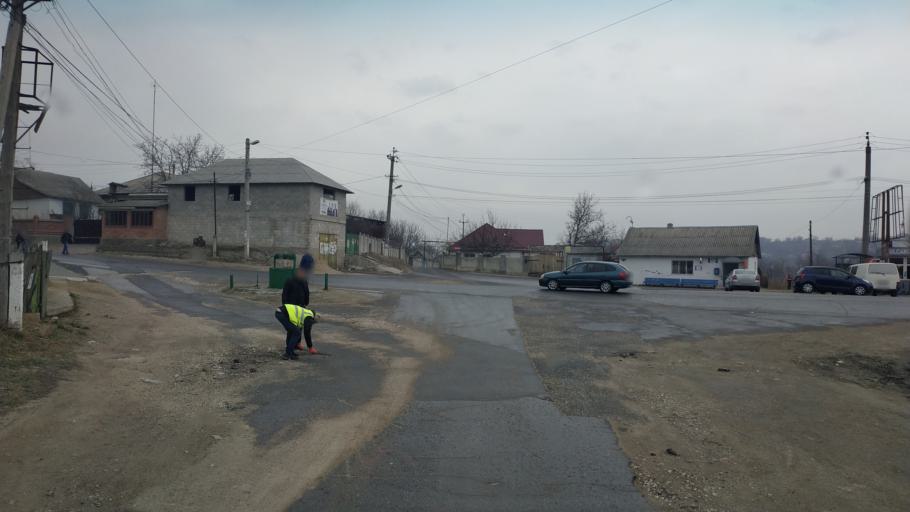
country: MD
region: Chisinau
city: Singera
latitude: 46.9160
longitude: 28.9737
